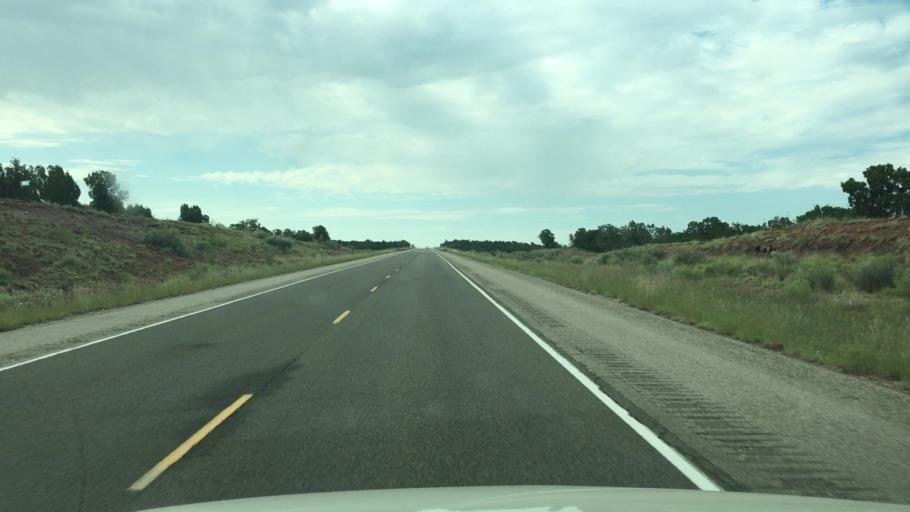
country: US
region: New Mexico
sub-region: Santa Fe County
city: Eldorado at Santa Fe
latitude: 35.2324
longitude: -105.8035
